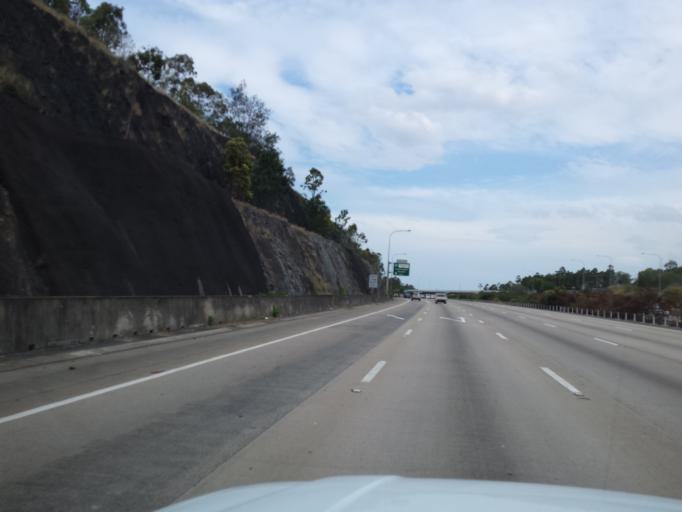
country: AU
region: Queensland
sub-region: Gold Coast
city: Upper Coomera
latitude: -27.9222
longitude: 153.3255
